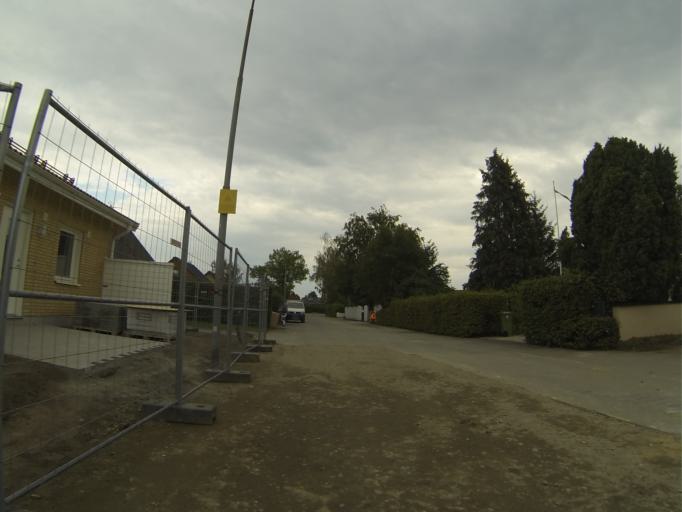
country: SE
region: Skane
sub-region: Staffanstorps Kommun
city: Staffanstorp
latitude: 55.6499
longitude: 13.2070
